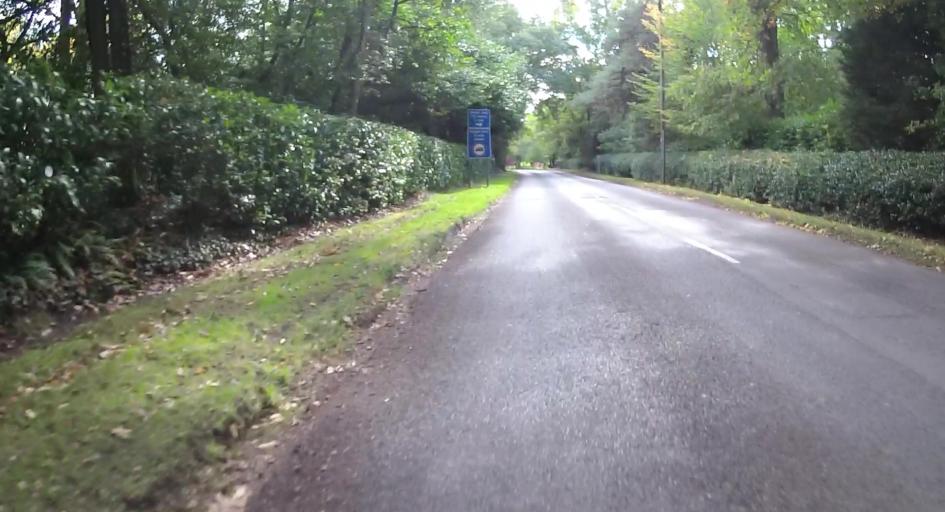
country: GB
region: England
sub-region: Surrey
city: Seale
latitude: 51.1954
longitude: -0.7458
